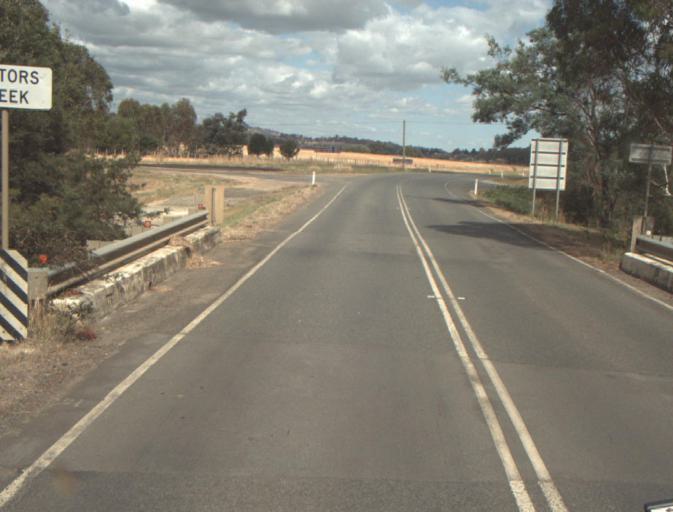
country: AU
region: Tasmania
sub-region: Launceston
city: Mayfield
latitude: -41.3078
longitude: 147.0497
